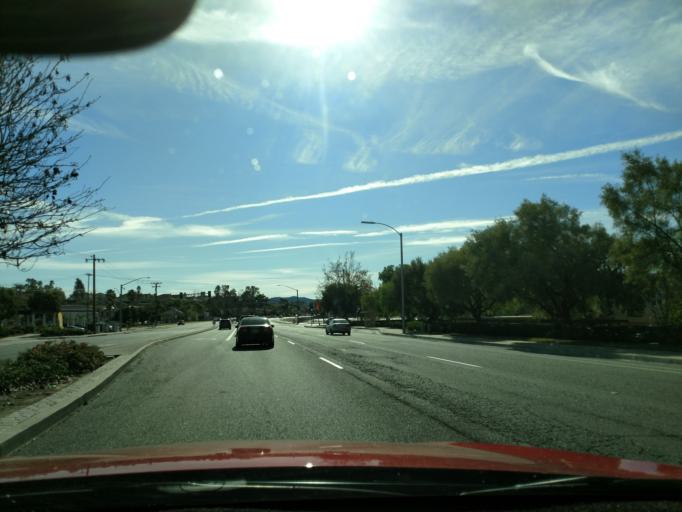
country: US
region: California
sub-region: Riverside County
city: Murrieta Hot Springs
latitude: 33.5405
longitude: -117.1444
